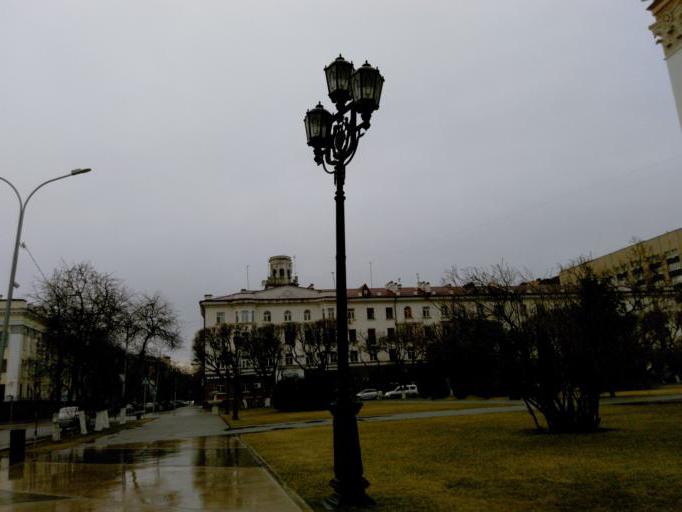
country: RU
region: Tjumen
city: Tyumen
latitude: 57.1541
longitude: 65.5427
